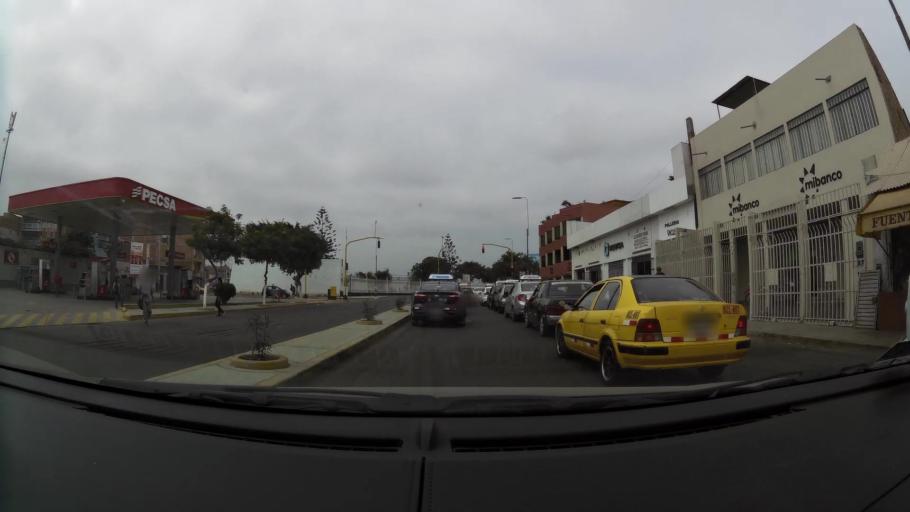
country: PE
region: La Libertad
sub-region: Provincia de Trujillo
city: Trujillo
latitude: -8.1056
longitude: -79.0271
